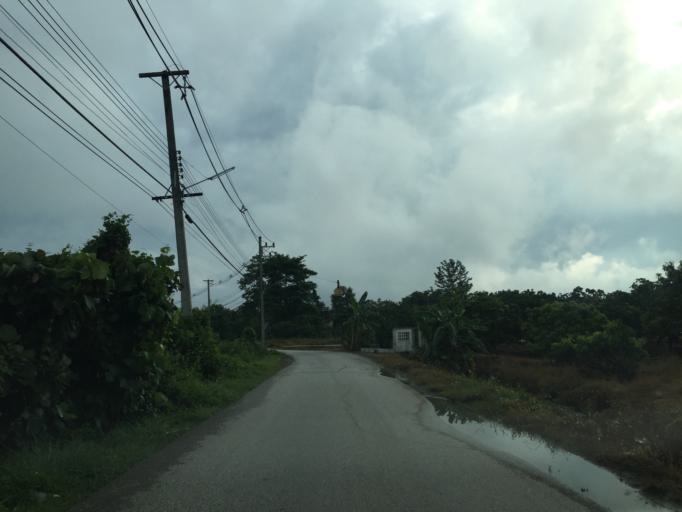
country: TH
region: Lamphun
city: Ban Thi
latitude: 18.6482
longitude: 99.0606
